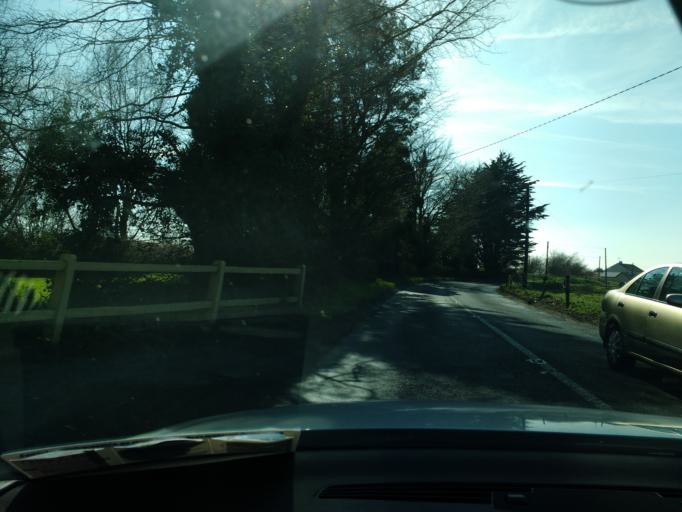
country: IE
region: Munster
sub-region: County Limerick
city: Castleconnell
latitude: 52.6982
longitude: -8.4612
